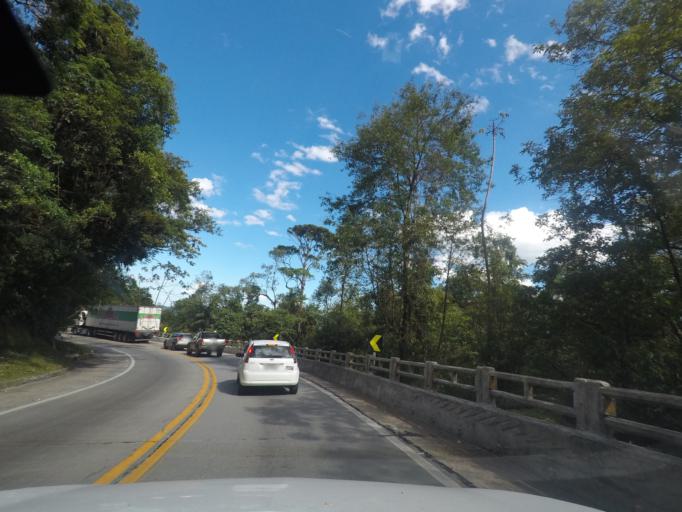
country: BR
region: Rio de Janeiro
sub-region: Guapimirim
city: Guapimirim
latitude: -22.4821
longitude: -42.9991
